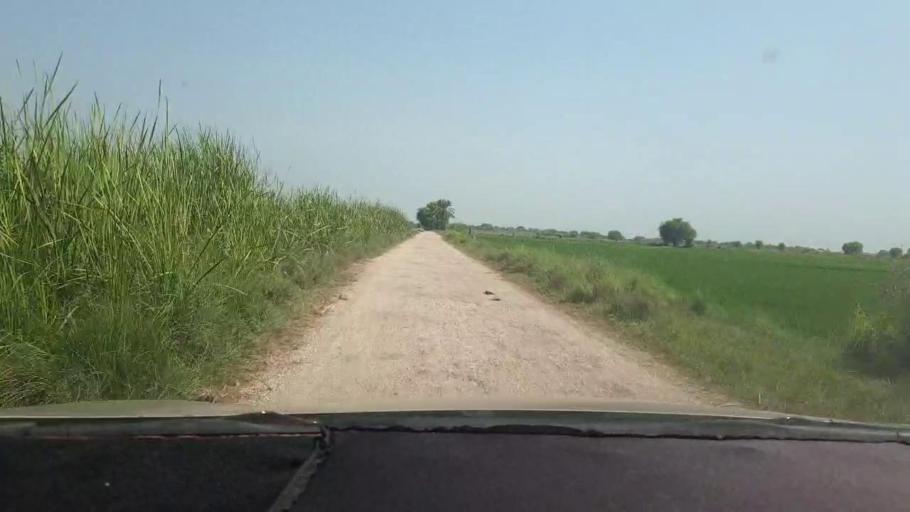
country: PK
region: Sindh
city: Miro Khan
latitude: 27.6991
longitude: 68.0926
